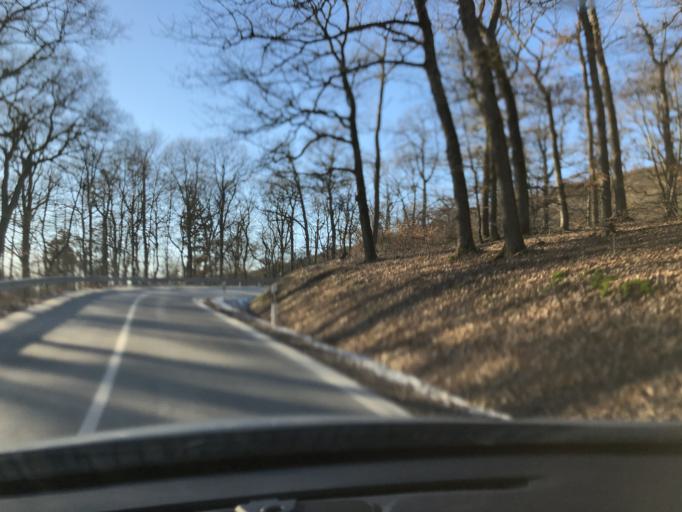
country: DE
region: Rheinland-Pfalz
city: Greimerath
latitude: 50.0139
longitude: 6.8975
